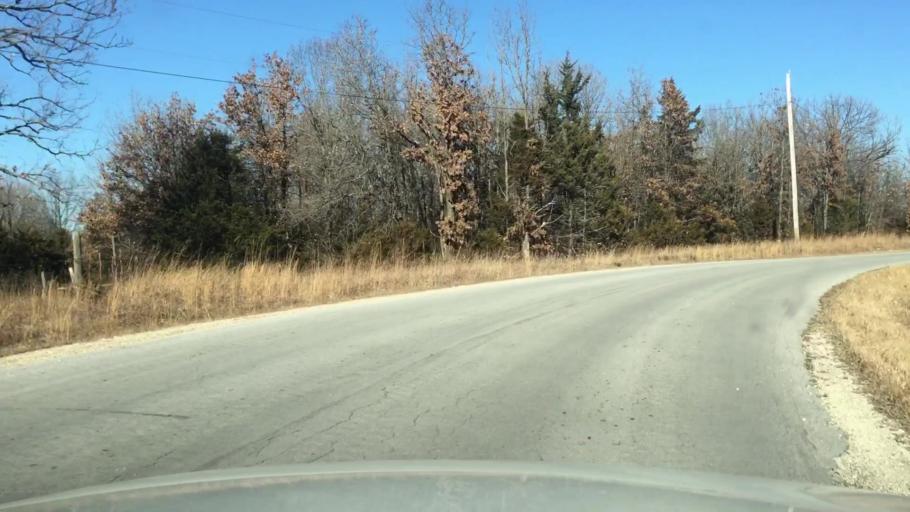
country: US
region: Missouri
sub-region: Morgan County
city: Versailles
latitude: 38.3491
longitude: -92.7489
